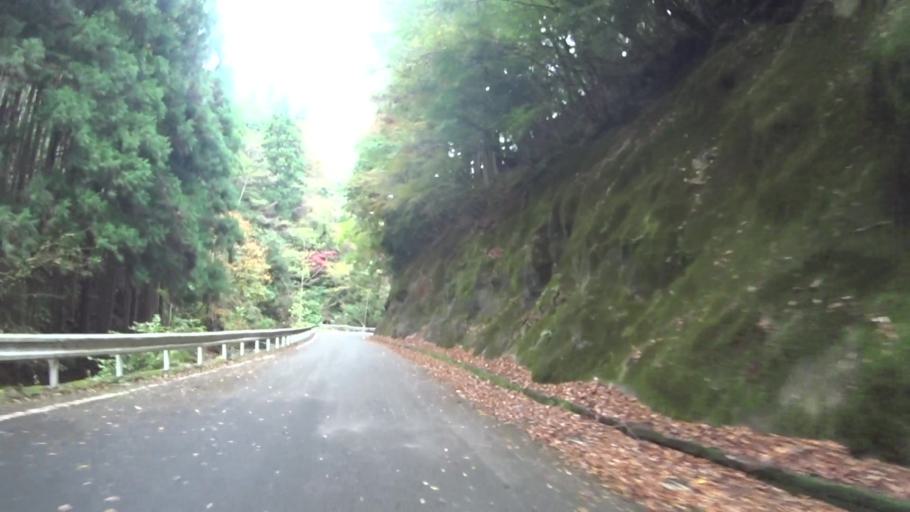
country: JP
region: Fukui
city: Obama
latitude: 35.2759
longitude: 135.7012
